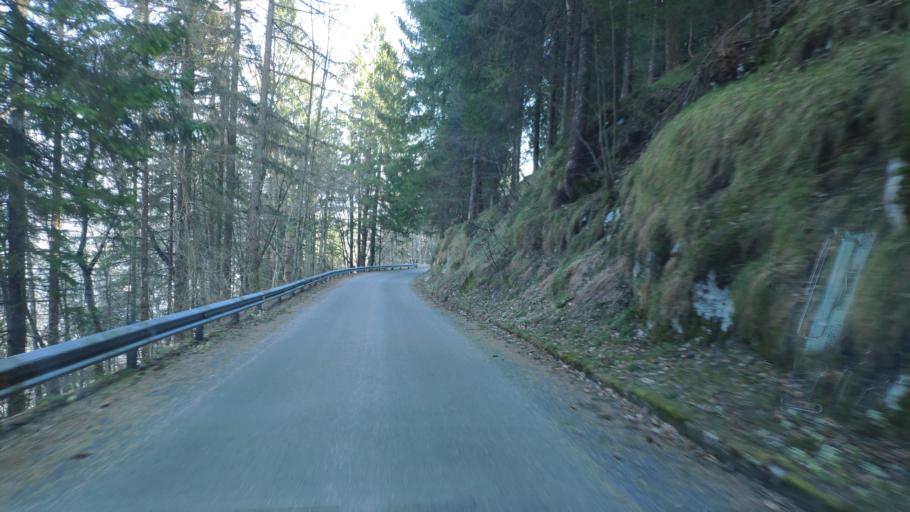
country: IT
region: Veneto
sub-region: Provincia di Vicenza
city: Enego
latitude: 45.9572
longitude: 11.6877
